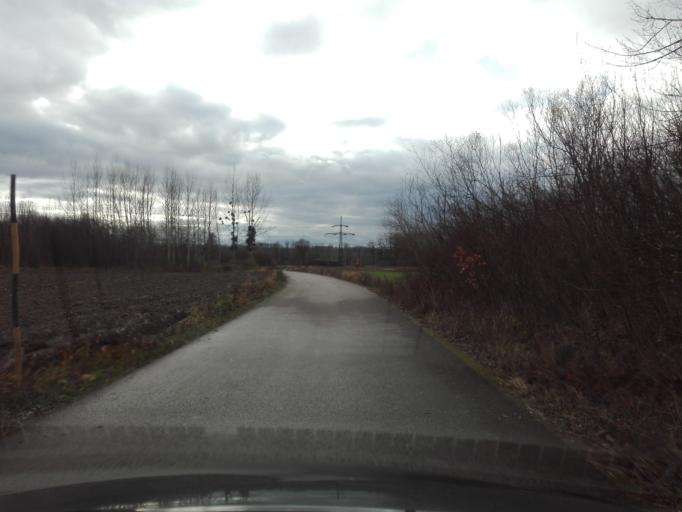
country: AT
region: Lower Austria
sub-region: Politischer Bezirk Amstetten
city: Strengberg
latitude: 48.1768
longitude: 14.6947
